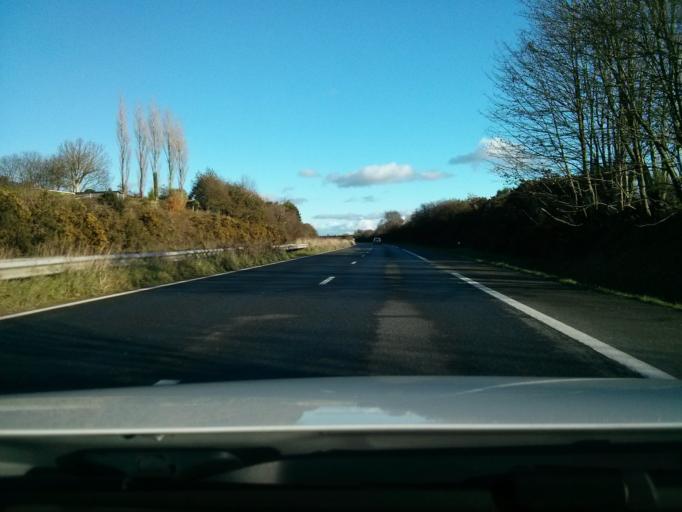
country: FR
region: Brittany
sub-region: Departement du Finistere
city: Plouedern
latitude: 48.4884
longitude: -4.2436
